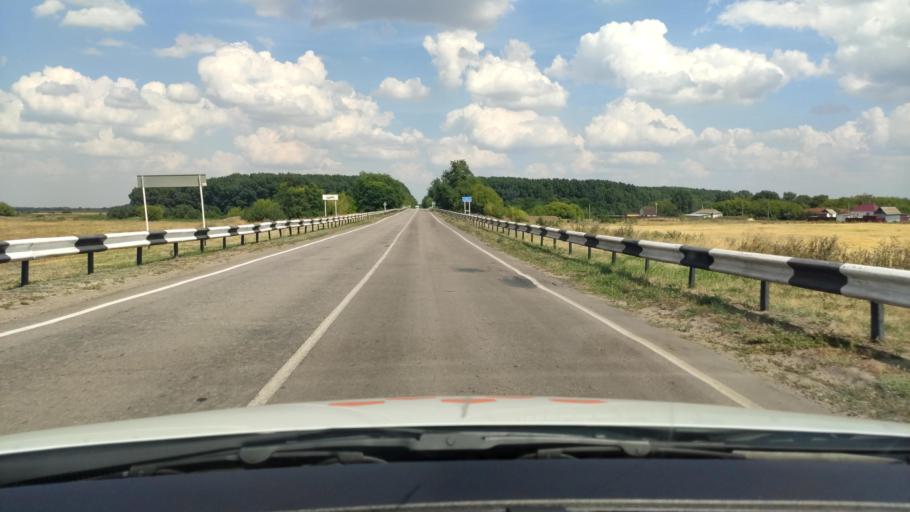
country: RU
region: Voronezj
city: Sadovoye
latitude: 51.7688
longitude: 40.4885
